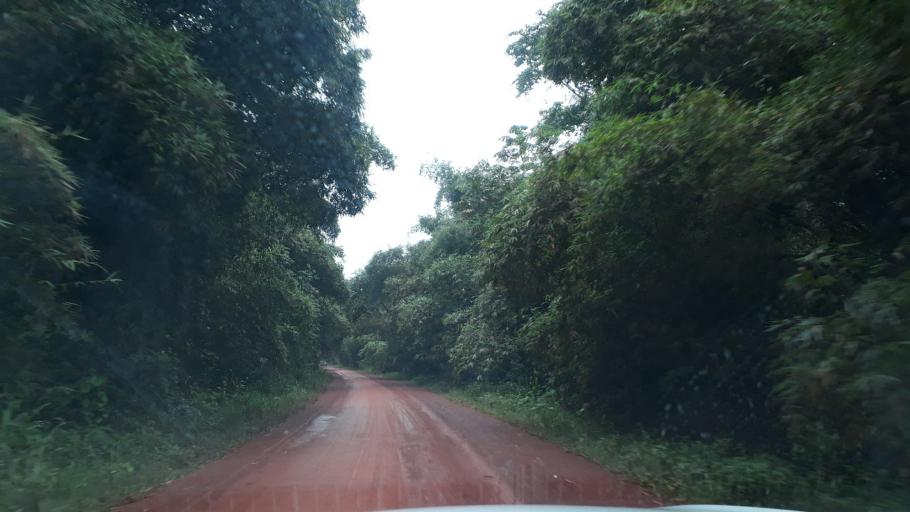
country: CD
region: Eastern Province
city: Wamba
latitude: 1.3752
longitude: 27.5975
